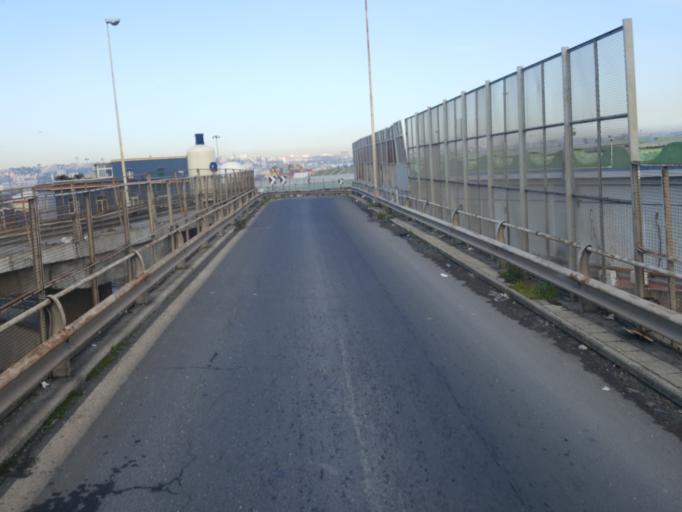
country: IT
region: Campania
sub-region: Provincia di Napoli
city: San Giorgio a Cremano
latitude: 40.8466
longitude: 14.3044
